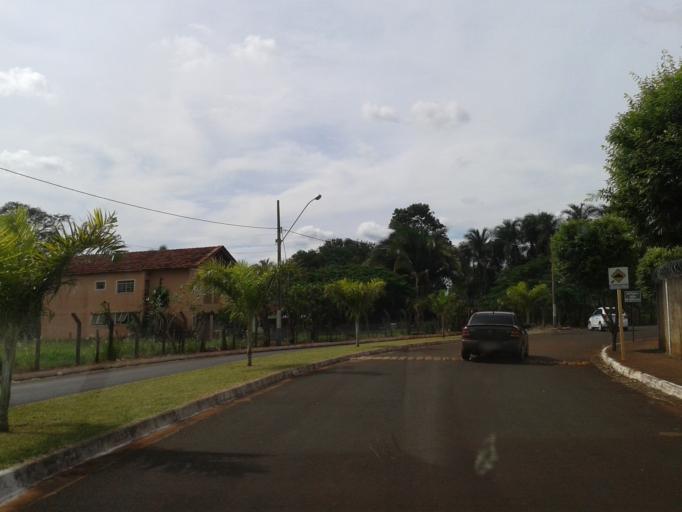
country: BR
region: Minas Gerais
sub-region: Centralina
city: Centralina
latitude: -18.5801
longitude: -49.2023
